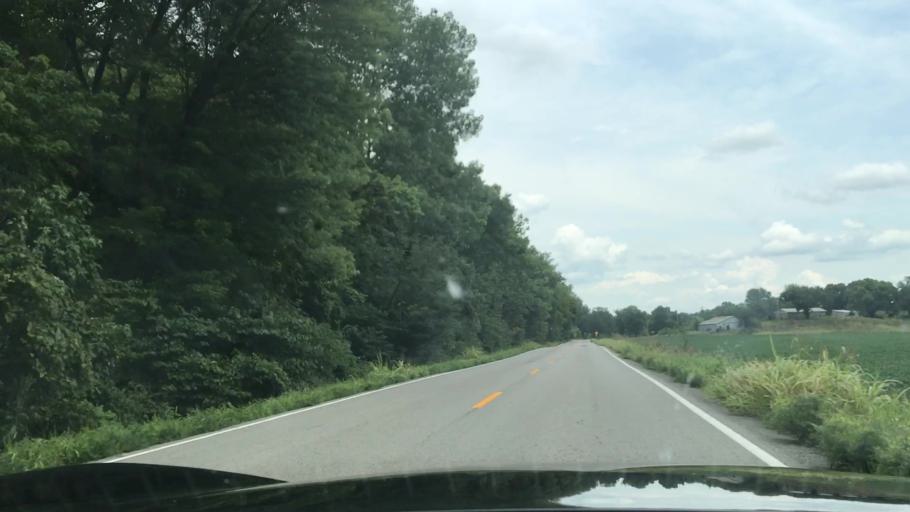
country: US
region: Kentucky
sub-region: Ohio County
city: Beaver Dam
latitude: 37.2139
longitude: -86.9070
